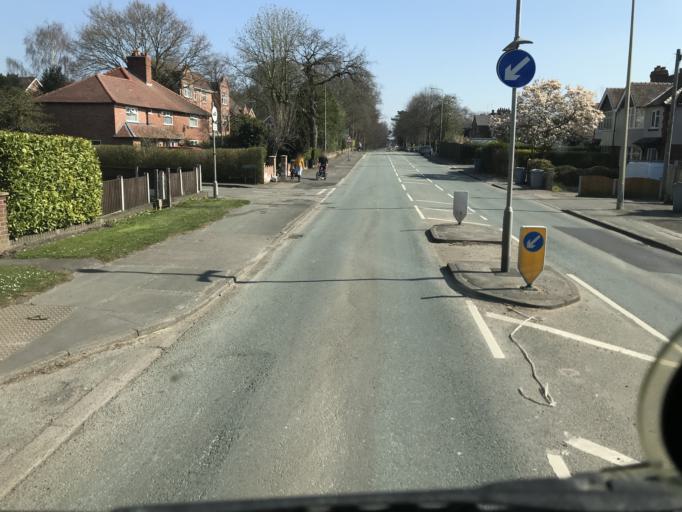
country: GB
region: England
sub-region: Cheshire East
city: Knutsford
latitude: 53.3034
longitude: -2.3846
